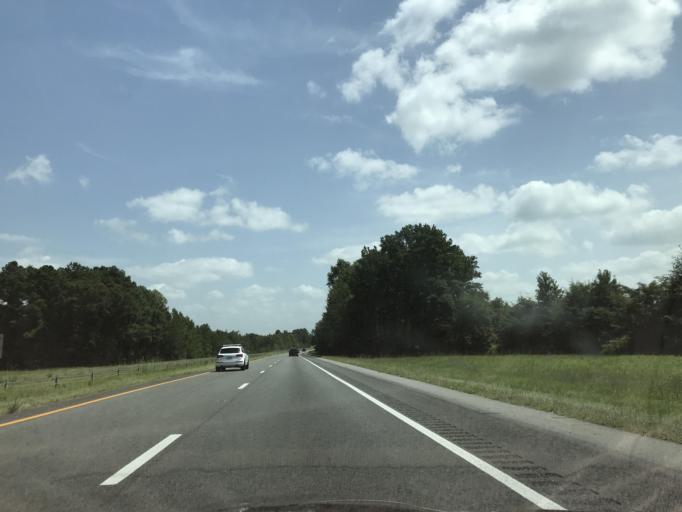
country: US
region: North Carolina
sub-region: Sampson County
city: Plain View
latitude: 35.2238
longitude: -78.3433
